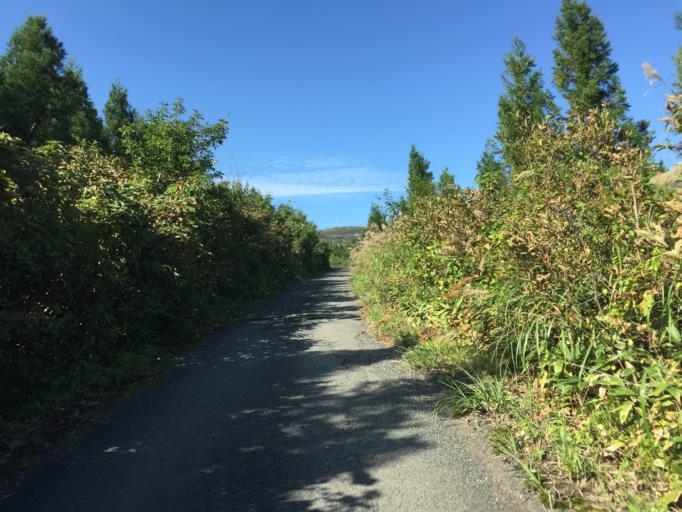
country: JP
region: Yamagata
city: Yonezawa
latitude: 37.8140
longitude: 140.2498
